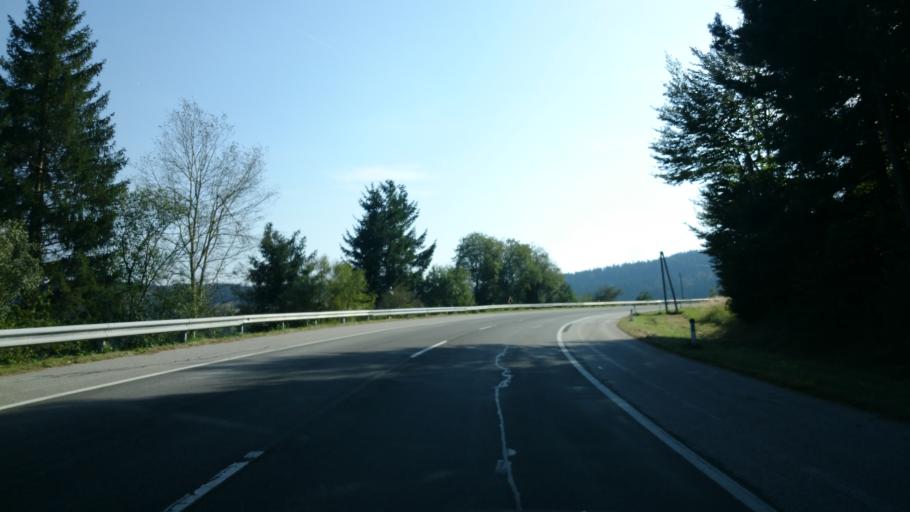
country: AT
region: Lower Austria
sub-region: Politischer Bezirk Neunkirchen
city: Monichkirchen
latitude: 47.5244
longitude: 16.0678
